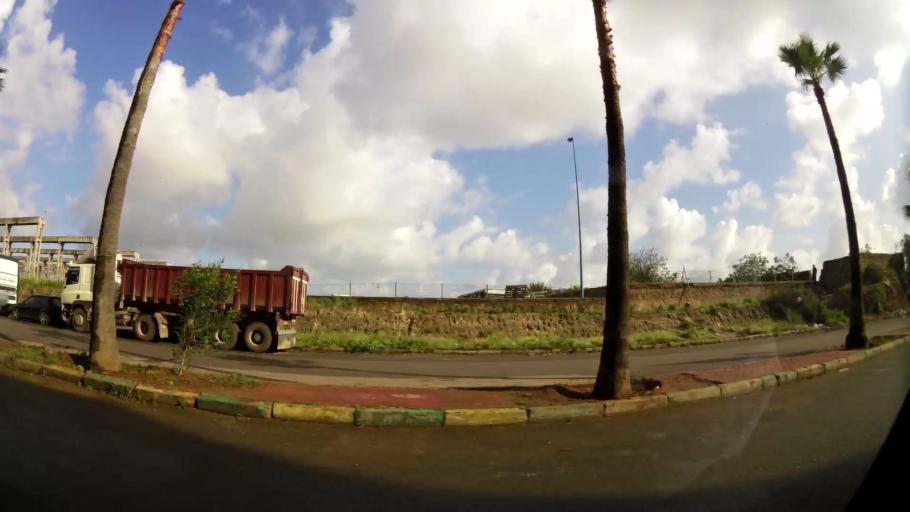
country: MA
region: Grand Casablanca
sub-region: Mediouna
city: Tit Mellil
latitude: 33.5970
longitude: -7.5380
